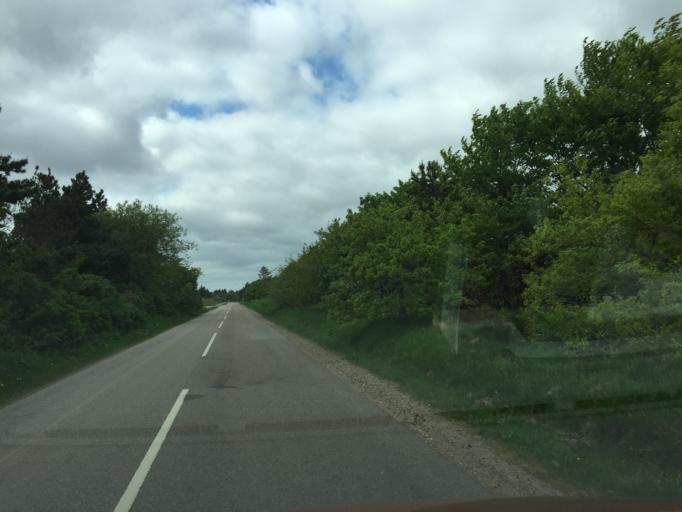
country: DK
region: Central Jutland
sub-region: Ringkobing-Skjern Kommune
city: Ringkobing
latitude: 55.9985
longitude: 8.3238
